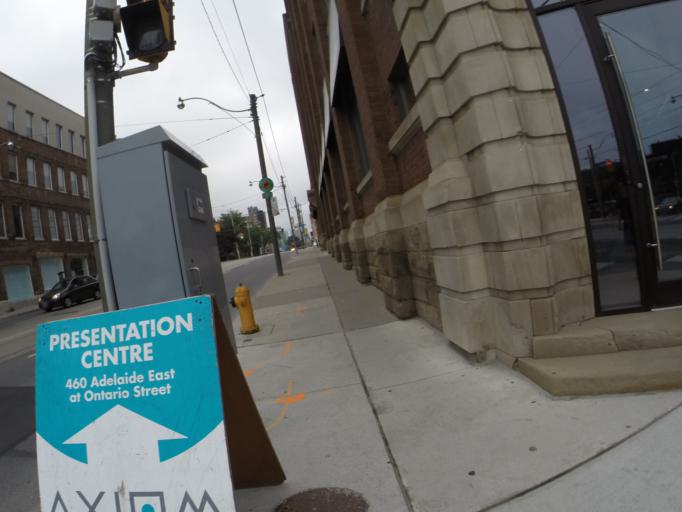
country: CA
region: Ontario
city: Toronto
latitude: 43.6518
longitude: -79.3629
